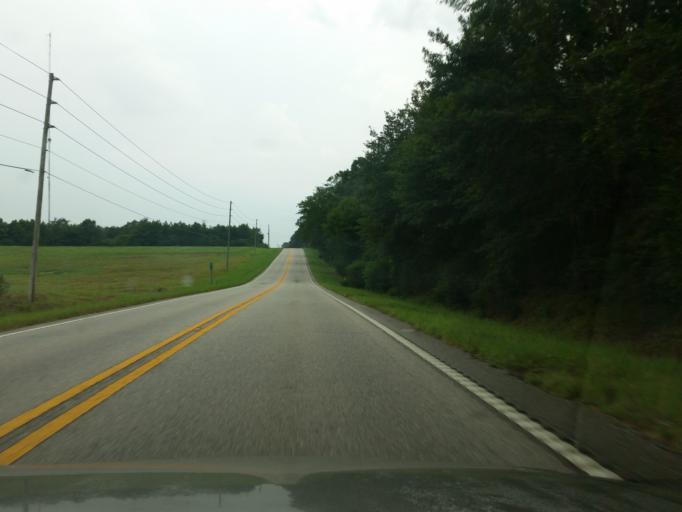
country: US
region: Alabama
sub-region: Baldwin County
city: Elberta
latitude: 30.5337
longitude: -87.5253
